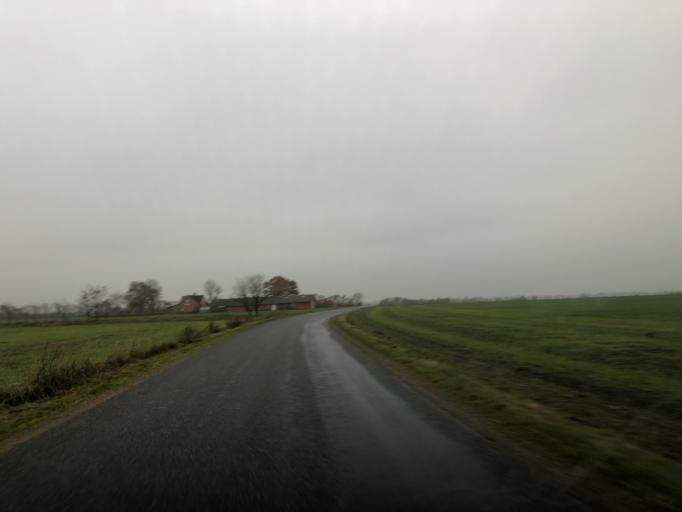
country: DK
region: Central Jutland
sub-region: Herning Kommune
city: Avlum
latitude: 56.2496
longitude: 8.8190
